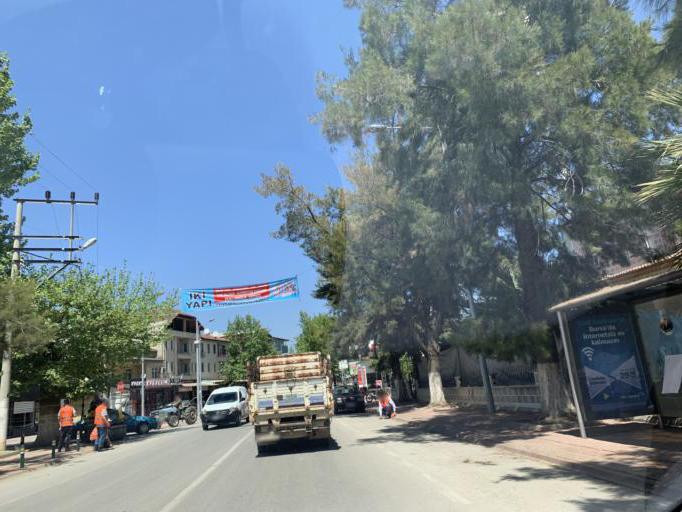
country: TR
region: Bursa
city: Iznik
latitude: 40.4239
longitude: 29.7196
